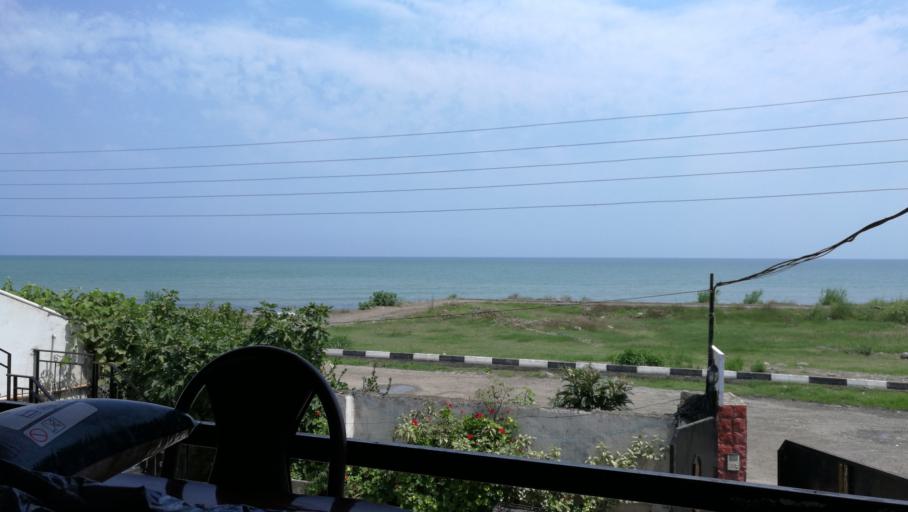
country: IR
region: Mazandaran
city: Ramsar
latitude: 36.9353
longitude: 50.6611
